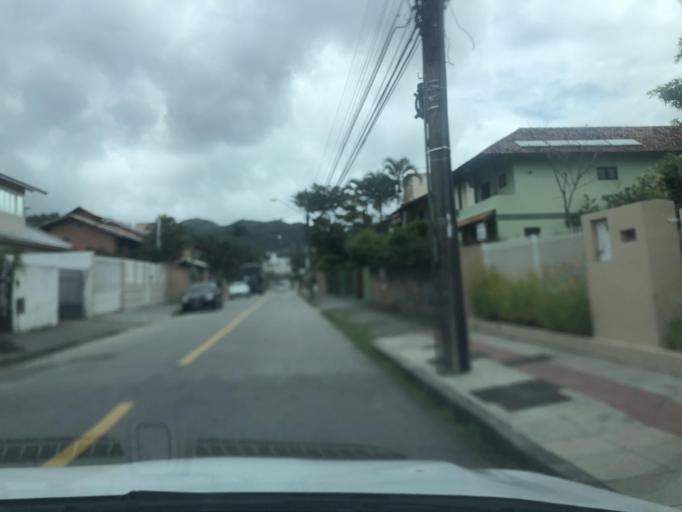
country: BR
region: Santa Catarina
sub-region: Florianopolis
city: Santa Monica
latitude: -27.5937
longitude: -48.5121
